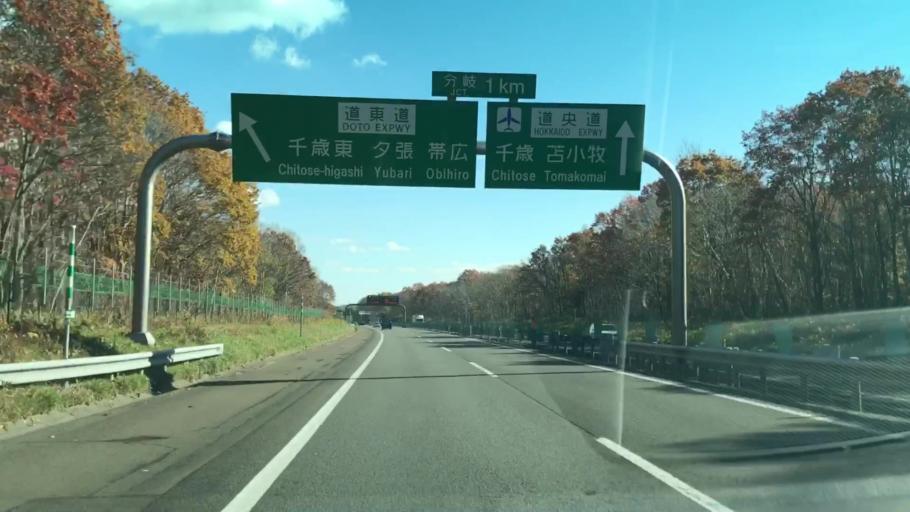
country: JP
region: Hokkaido
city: Chitose
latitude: 42.8502
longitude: 141.5718
